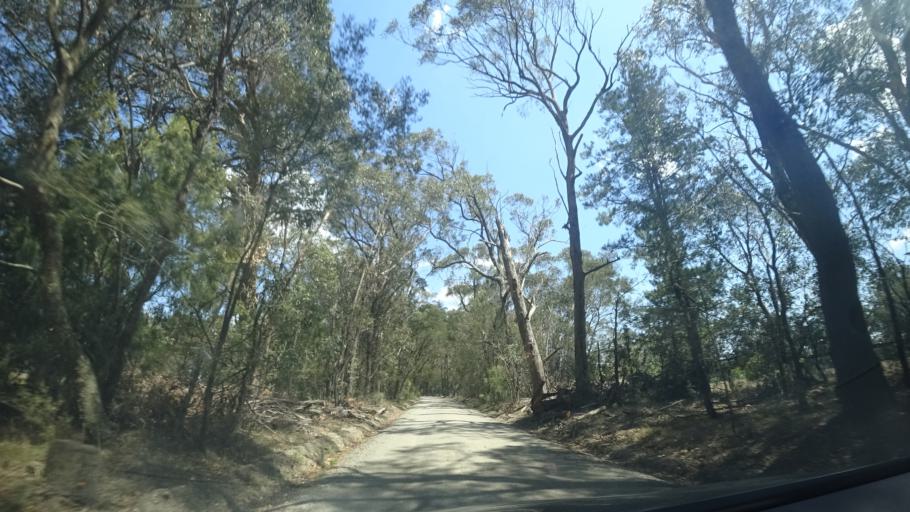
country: AU
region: New South Wales
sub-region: Wingecarribee
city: Bundanoon
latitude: -34.6346
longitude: 150.2558
